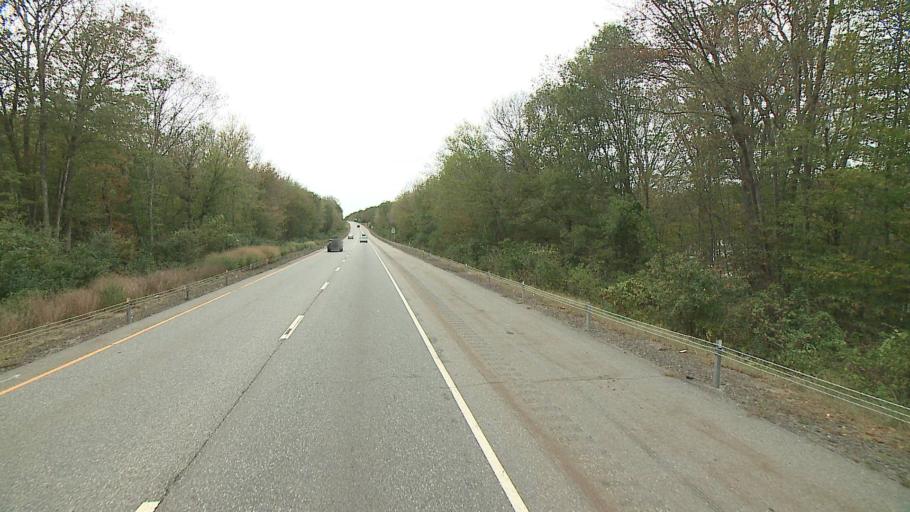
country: US
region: Connecticut
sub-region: Middlesex County
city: Deep River Center
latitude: 41.3849
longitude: -72.4498
